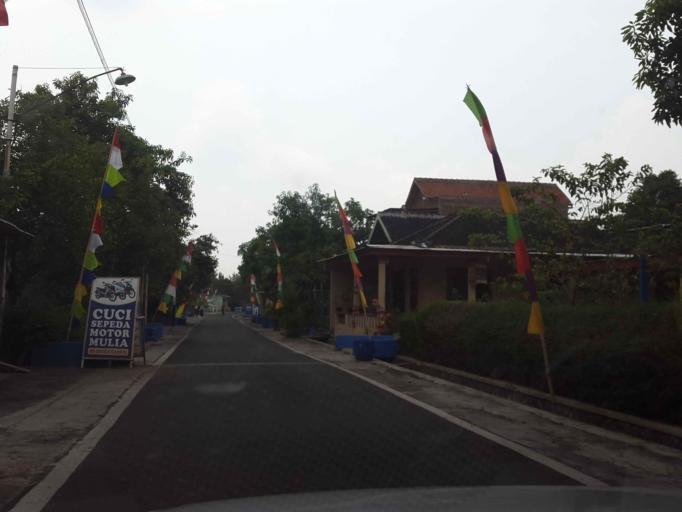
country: ID
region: Central Java
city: Jaten
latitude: -7.6006
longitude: 110.9538
